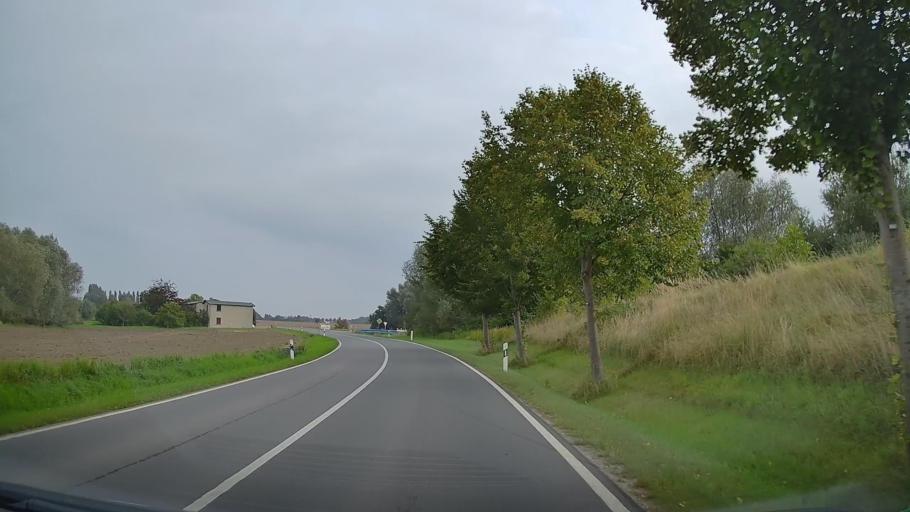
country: DE
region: Mecklenburg-Vorpommern
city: Ostseebad Kuhlungsborn
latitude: 54.1352
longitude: 11.7605
